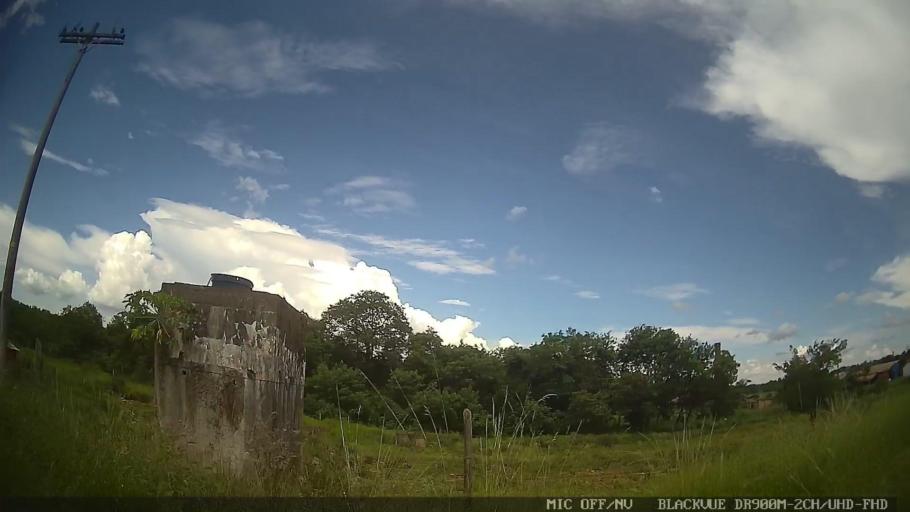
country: BR
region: Sao Paulo
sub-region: Conchas
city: Conchas
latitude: -23.0130
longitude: -48.0035
